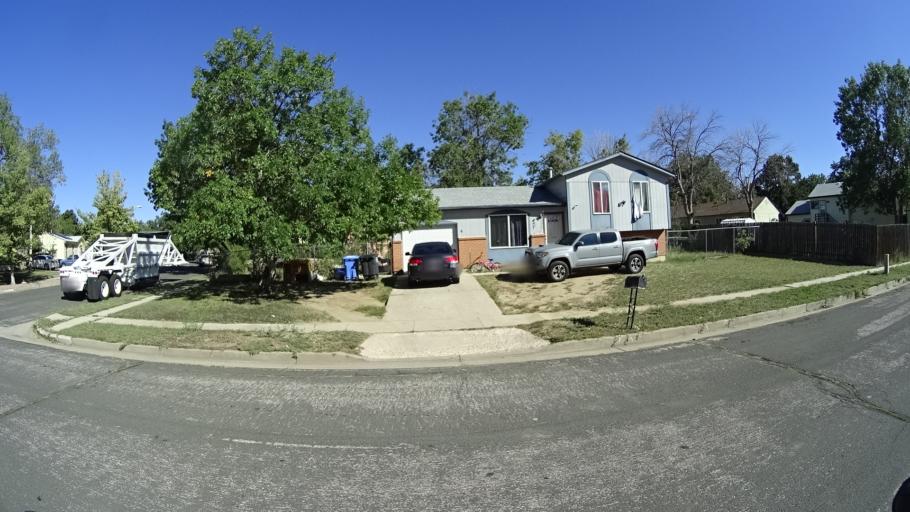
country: US
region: Colorado
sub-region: El Paso County
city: Stratmoor
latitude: 38.7956
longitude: -104.7532
